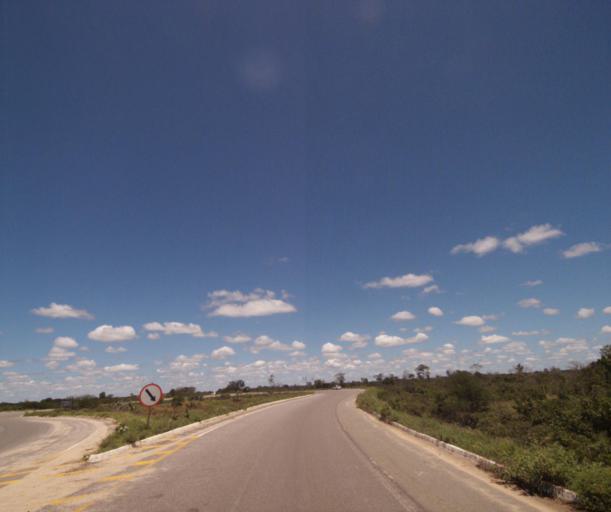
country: BR
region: Bahia
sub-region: Carinhanha
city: Carinhanha
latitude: -14.2880
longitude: -43.7827
